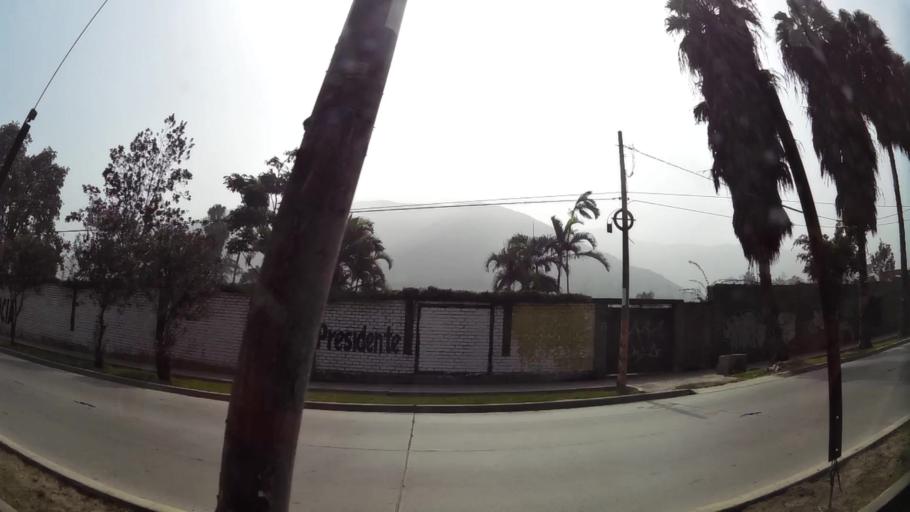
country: PE
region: Lima
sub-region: Lima
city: Chosica
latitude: -11.9481
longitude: -76.7183
